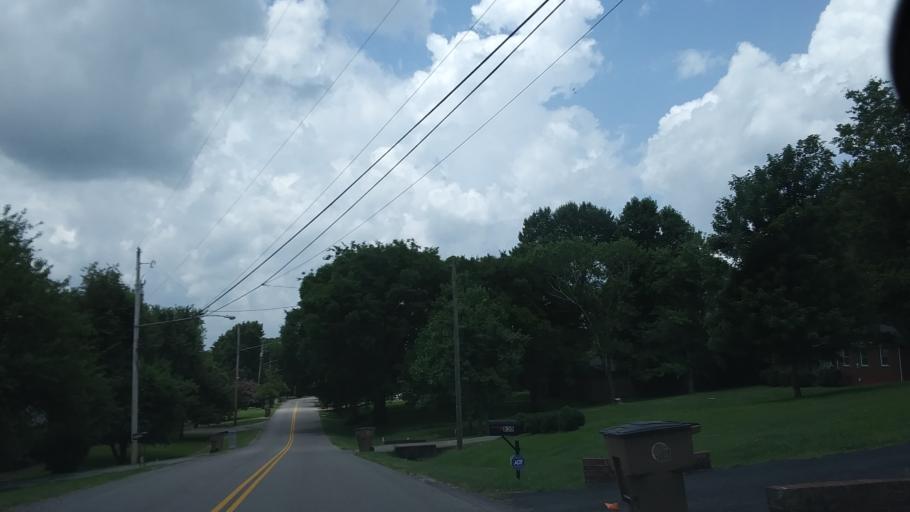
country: US
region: Tennessee
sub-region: Davidson County
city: Belle Meade
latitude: 36.1351
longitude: -86.8796
